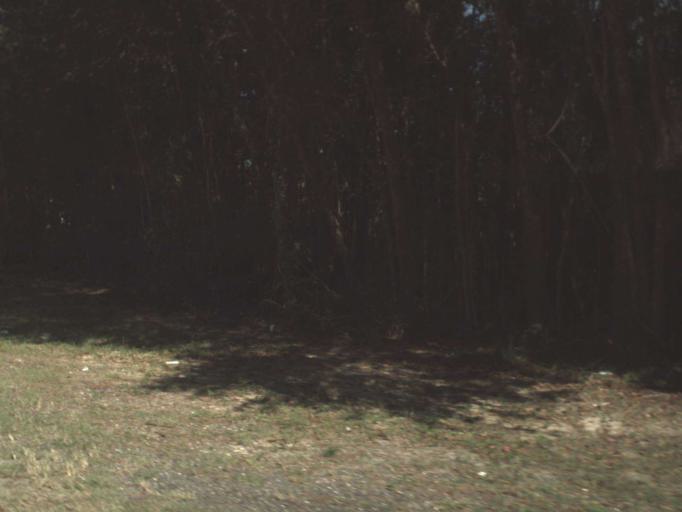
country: US
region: Alabama
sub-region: Covington County
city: Florala
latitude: 30.9943
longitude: -86.3340
